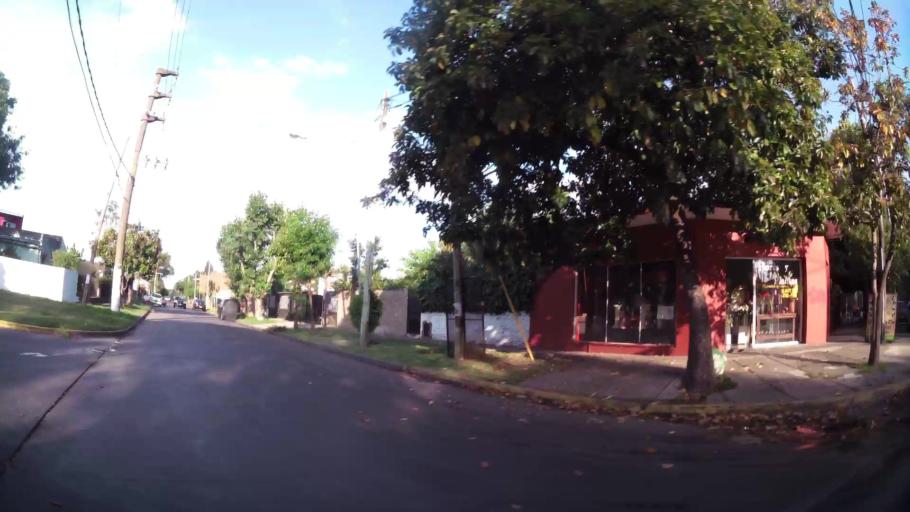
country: AR
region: Buenos Aires
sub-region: Partido de Tigre
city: Tigre
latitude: -34.4539
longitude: -58.6340
